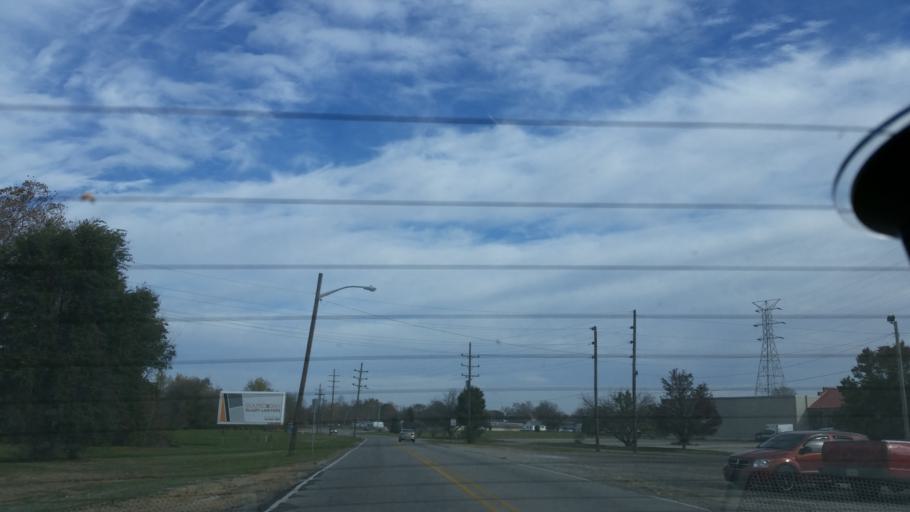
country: US
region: Indiana
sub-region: Howard County
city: Kokomo
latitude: 40.4768
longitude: -86.1483
